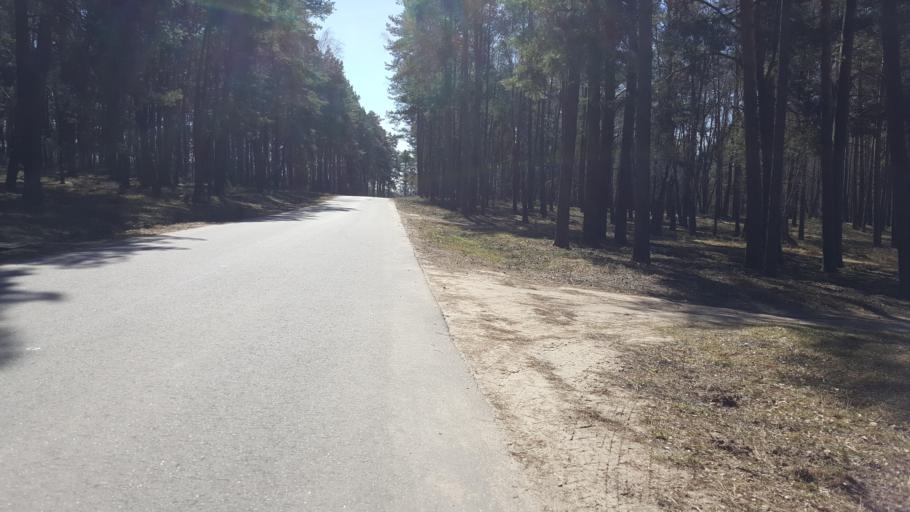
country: BY
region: Brest
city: Kamyanyets
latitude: 52.3502
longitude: 23.8271
